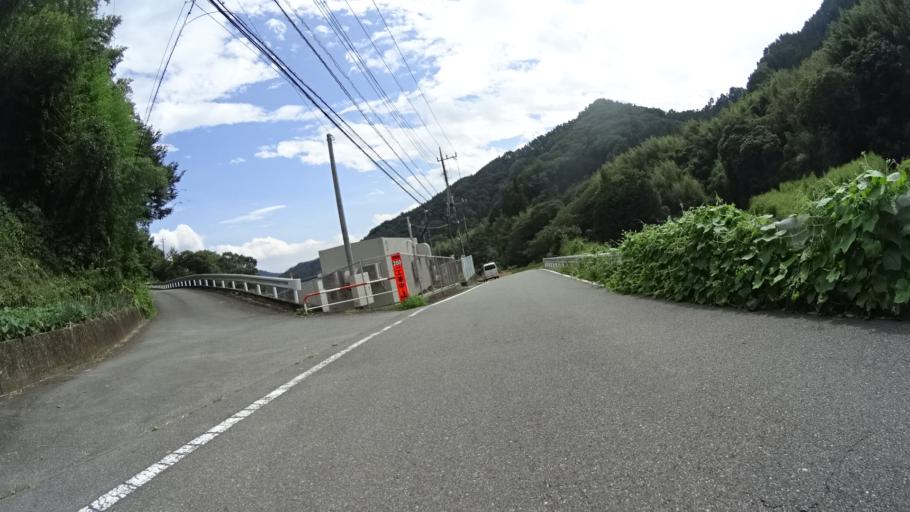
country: JP
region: Yamanashi
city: Nirasaki
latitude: 35.7665
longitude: 138.5336
